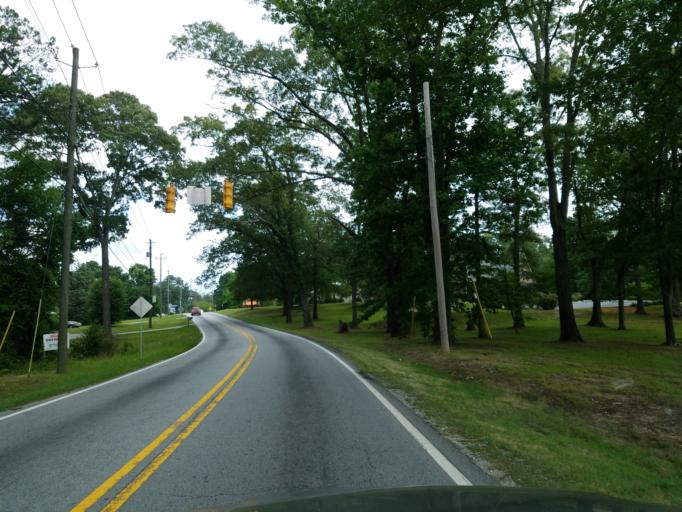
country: US
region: Georgia
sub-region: Douglas County
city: Lithia Springs
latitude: 33.7792
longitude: -84.6549
